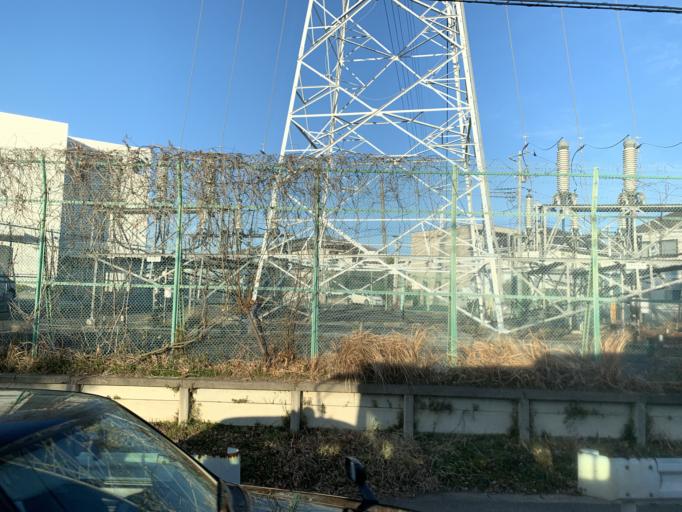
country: JP
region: Chiba
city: Kashiwa
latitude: 35.8682
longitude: 139.9561
